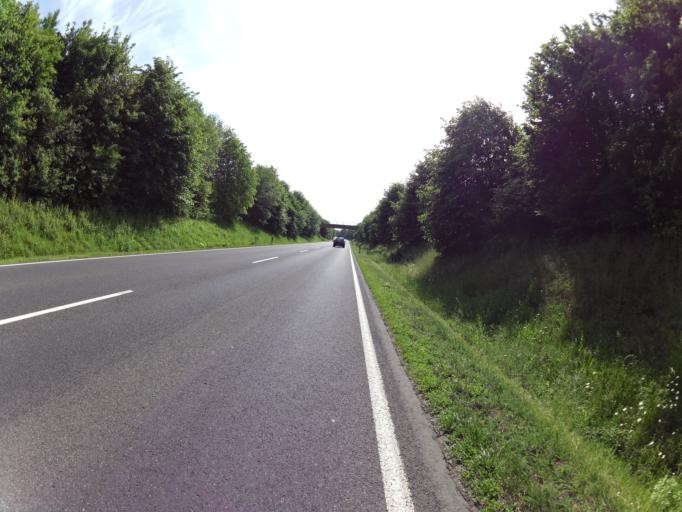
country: DE
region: North Rhine-Westphalia
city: Julich
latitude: 50.9076
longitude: 6.3239
